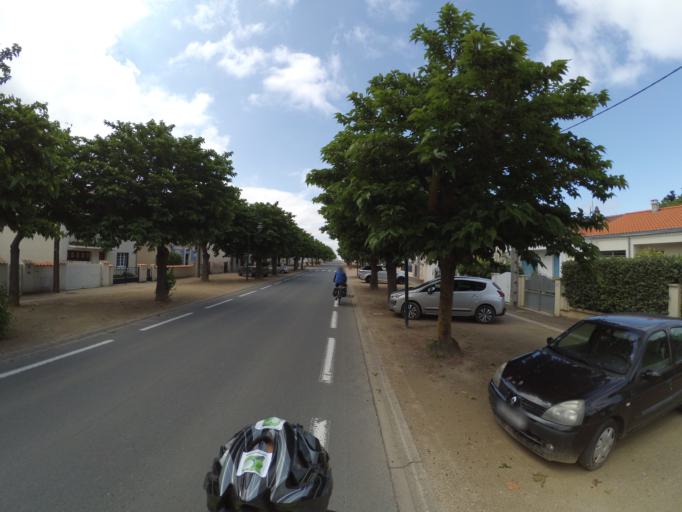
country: FR
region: Poitou-Charentes
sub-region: Departement de la Charente-Maritime
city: Chatelaillon-Plage
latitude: 46.0647
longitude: -1.0919
